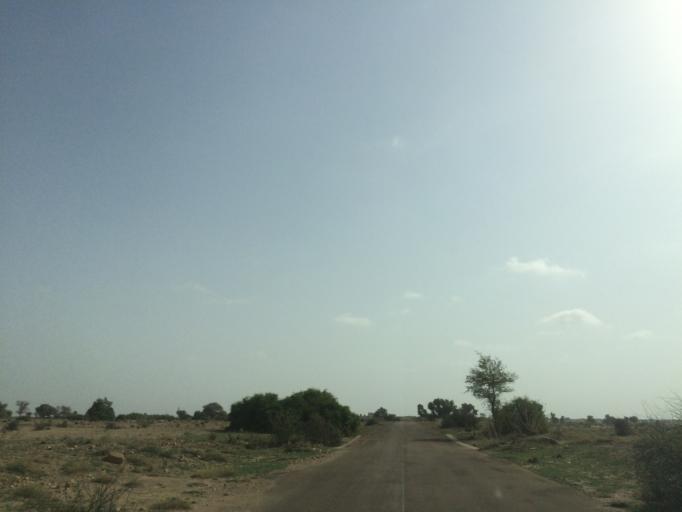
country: IN
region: Rajasthan
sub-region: Jaisalmer
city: Jaisalmer
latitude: 26.8086
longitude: 70.6977
